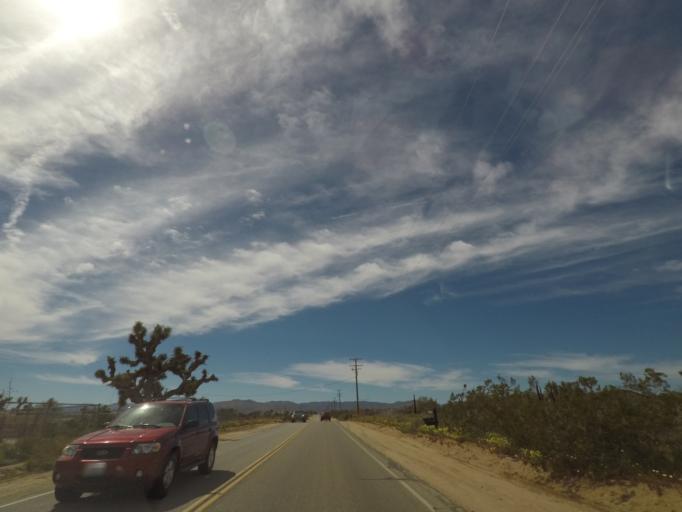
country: US
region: California
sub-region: San Bernardino County
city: Joshua Tree
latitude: 34.1812
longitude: -116.3696
